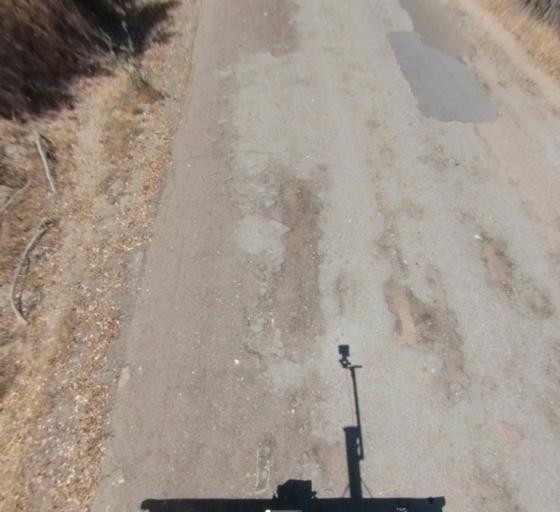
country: US
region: California
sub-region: Fresno County
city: Auberry
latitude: 37.1527
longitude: -119.4367
